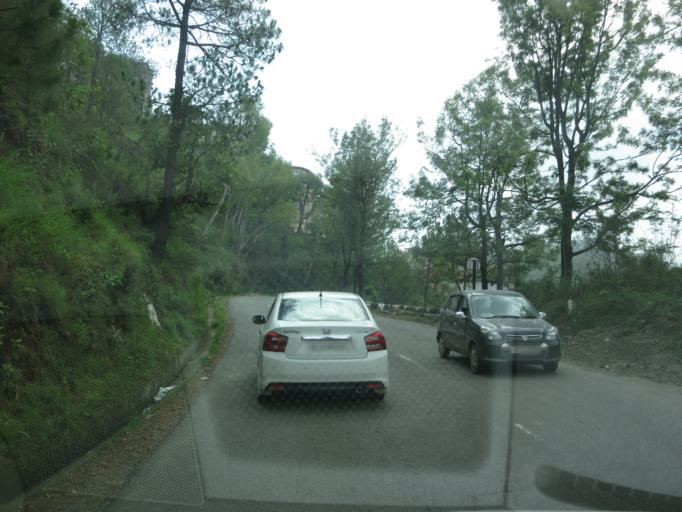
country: IN
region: Himachal Pradesh
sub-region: Solan
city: Dagshai
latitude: 30.8888
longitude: 77.0719
